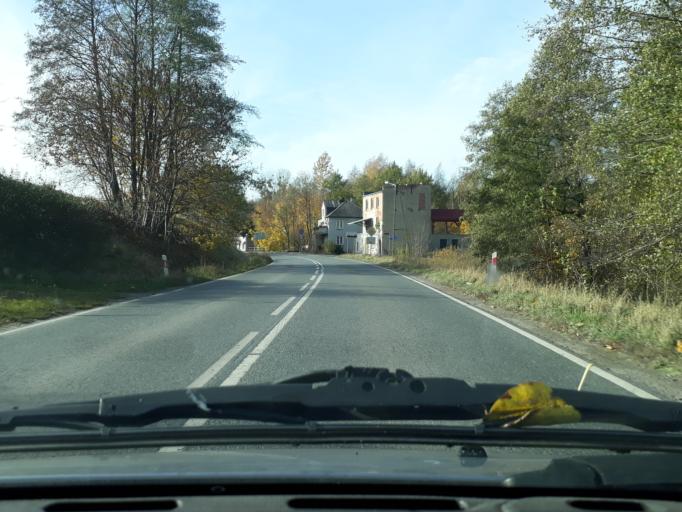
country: PL
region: Silesian Voivodeship
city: Wozniki
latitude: 50.5918
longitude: 19.0692
